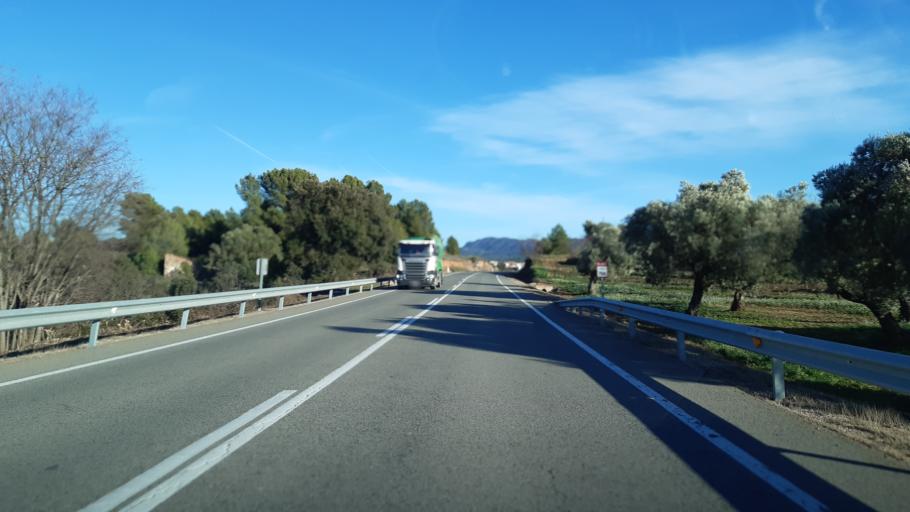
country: ES
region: Catalonia
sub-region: Provincia de Tarragona
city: Gandesa
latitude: 41.0545
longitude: 0.4140
